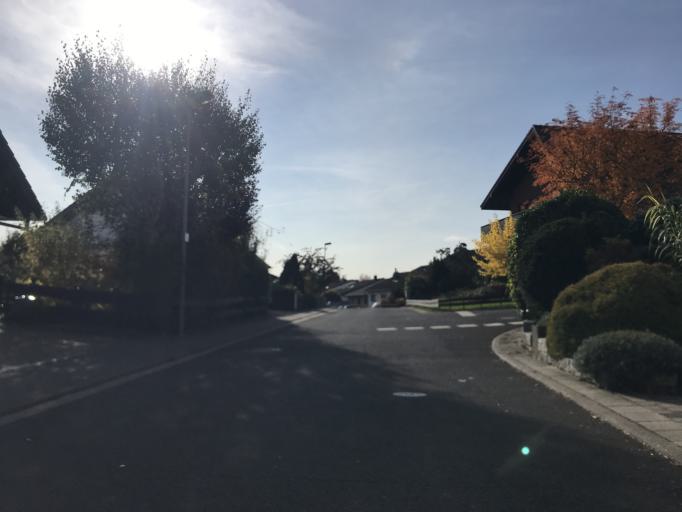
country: DE
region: Rheinland-Pfalz
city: Essenheim
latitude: 49.9266
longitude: 8.1546
